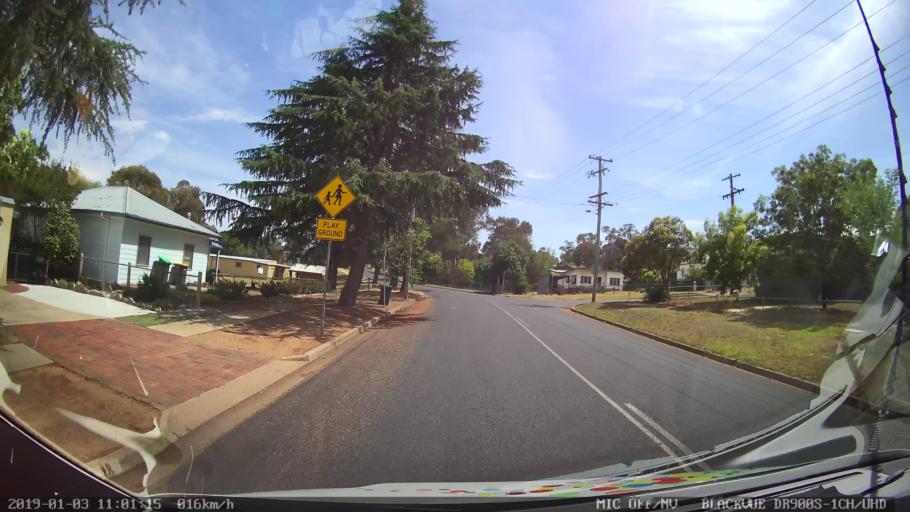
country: AU
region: New South Wales
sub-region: Young
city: Young
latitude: -34.3063
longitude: 148.2994
